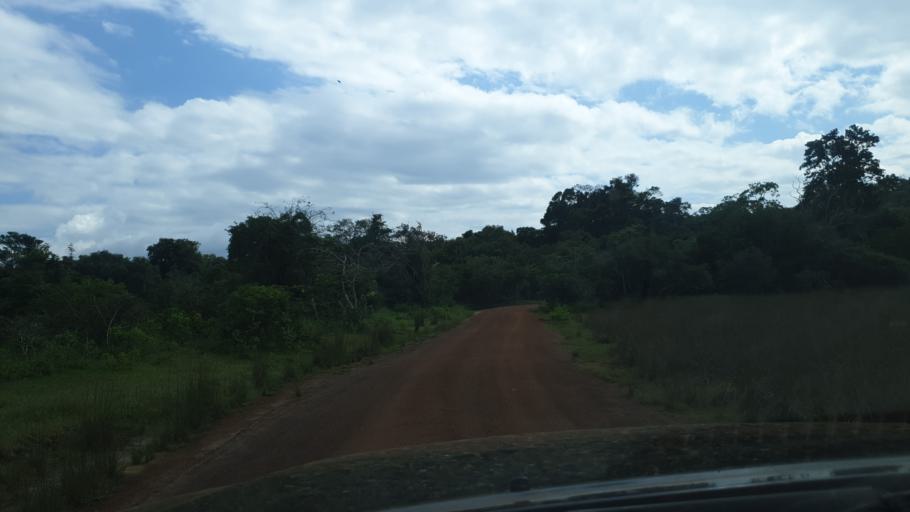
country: LK
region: North Central
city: Anuradhapura
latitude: 8.4241
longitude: 80.0241
